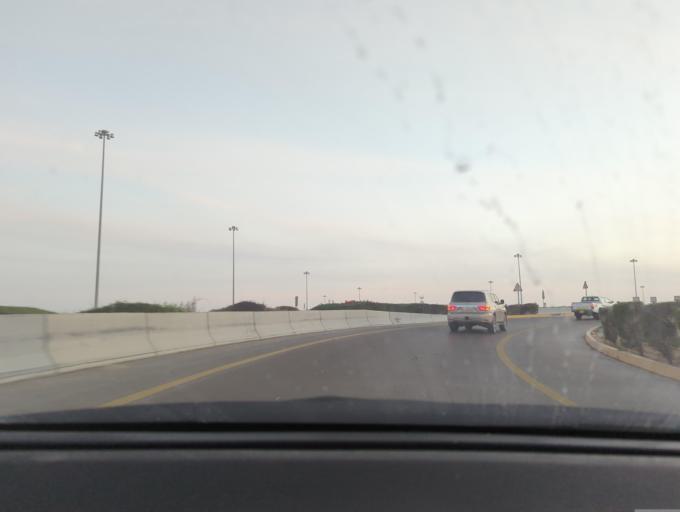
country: AE
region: Abu Dhabi
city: Abu Dhabi
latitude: 24.3768
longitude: 54.5532
